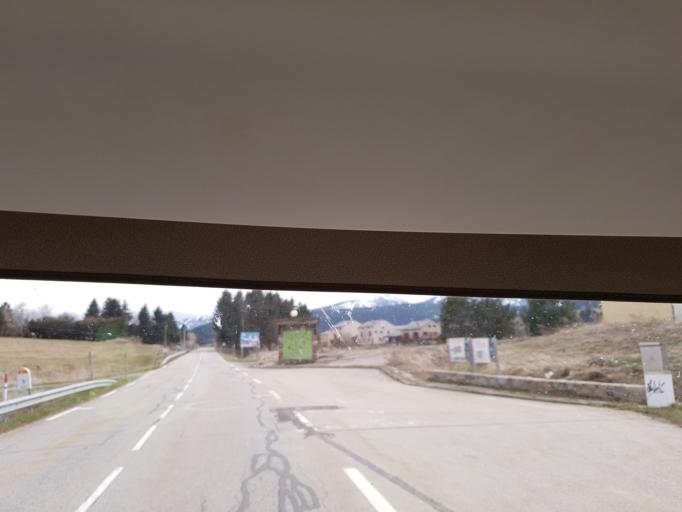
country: ES
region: Catalonia
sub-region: Provincia de Girona
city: Llivia
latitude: 42.6483
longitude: 2.1172
